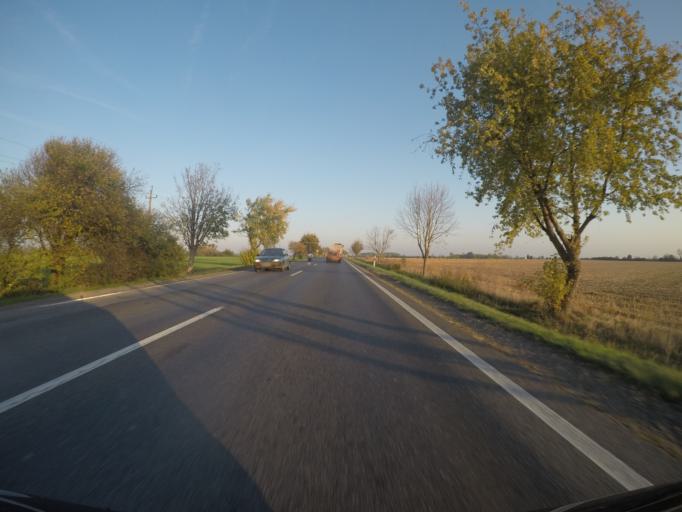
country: HU
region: Baranya
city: Szentlorinc
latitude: 46.0417
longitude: 17.9223
